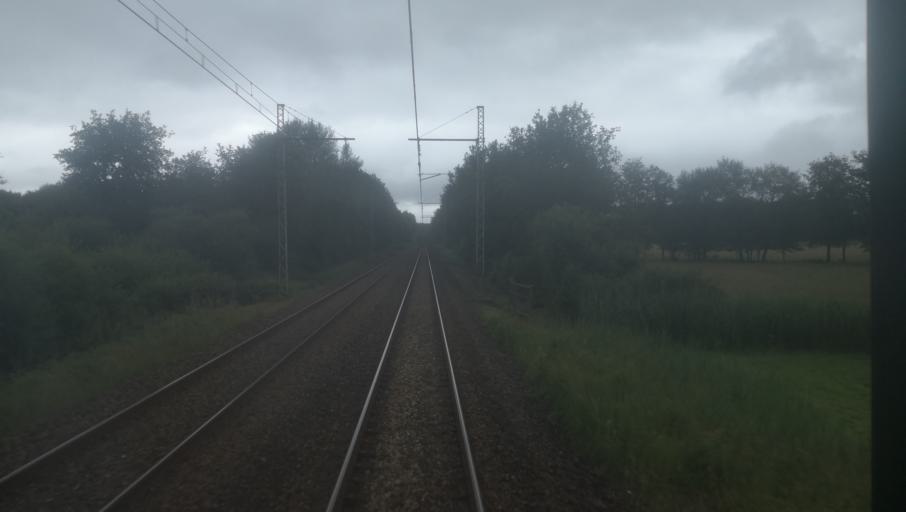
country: FR
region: Centre
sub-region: Departement de l'Indre
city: Luant
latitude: 46.7211
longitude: 1.5811
